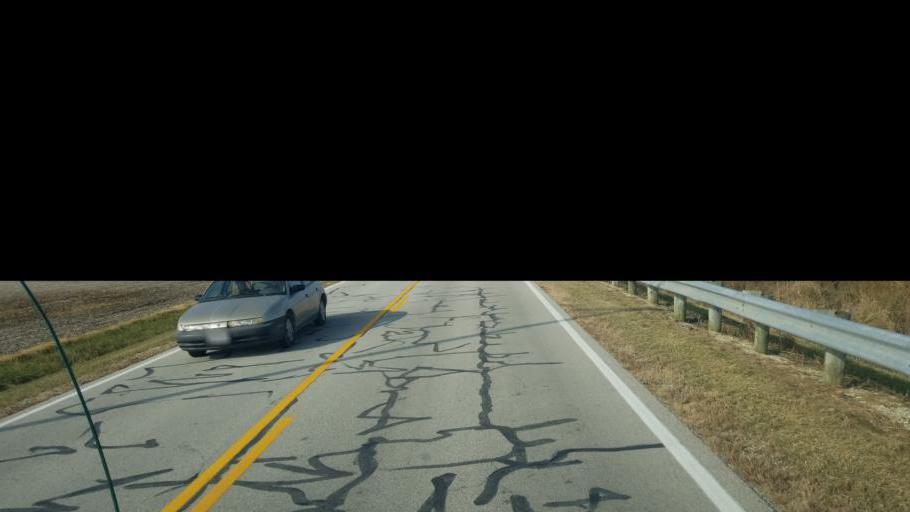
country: US
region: Ohio
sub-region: Mercer County
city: Celina
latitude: 40.5754
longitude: -84.6008
